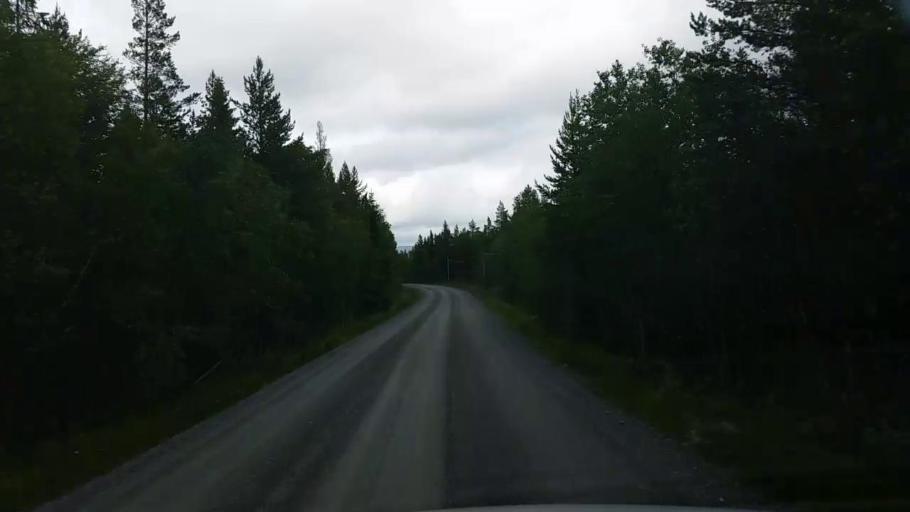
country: NO
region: Hedmark
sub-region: Engerdal
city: Engerdal
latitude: 62.4058
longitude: 12.6655
